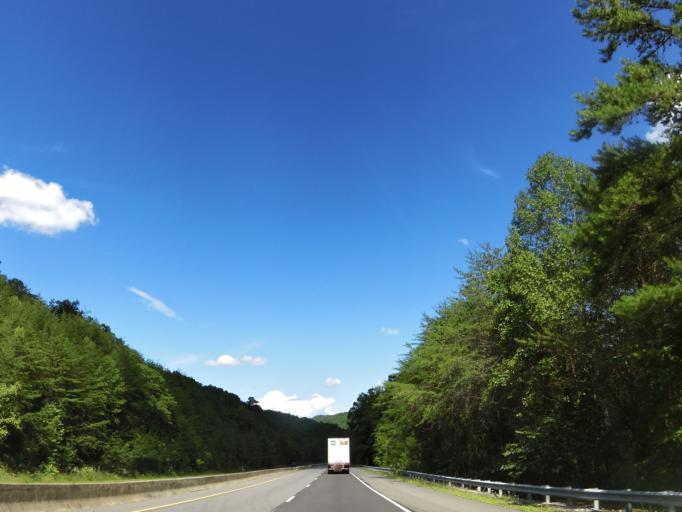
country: US
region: Tennessee
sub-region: Grainger County
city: Bean Station
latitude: 36.3595
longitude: -83.3498
